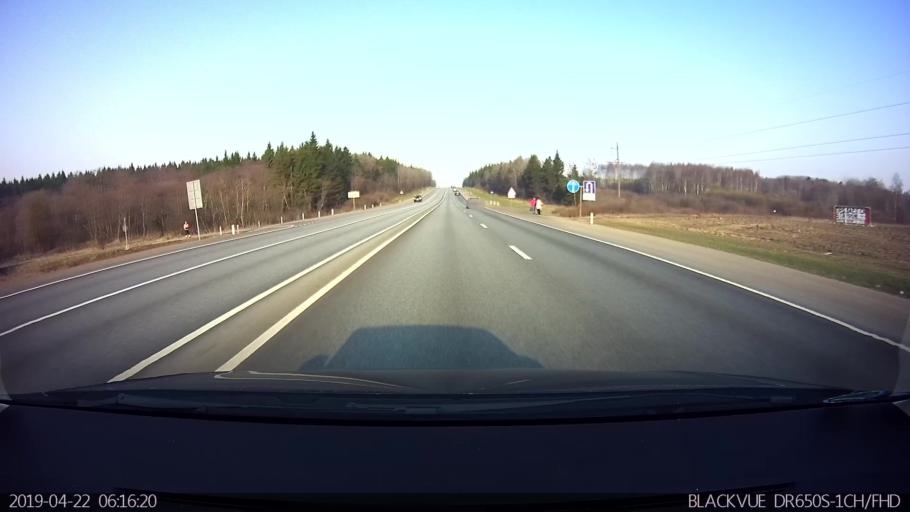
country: RU
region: Moskovskaya
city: Mozhaysk
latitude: 55.4600
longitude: 36.0221
